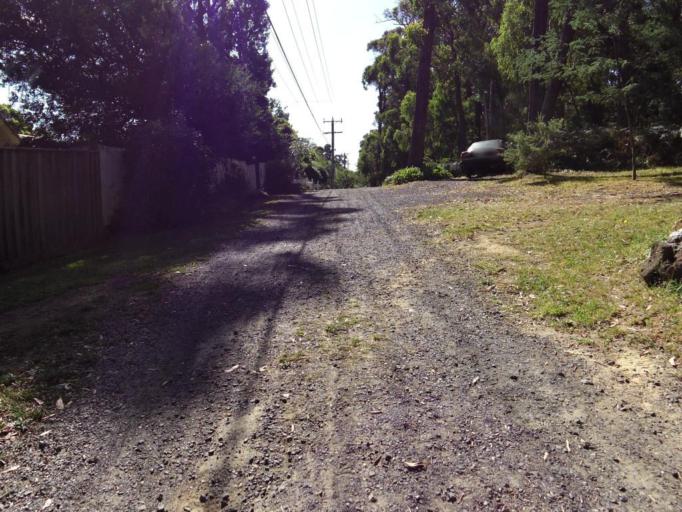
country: AU
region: Victoria
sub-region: Yarra Ranges
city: Montrose
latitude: -37.8036
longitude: 145.3464
